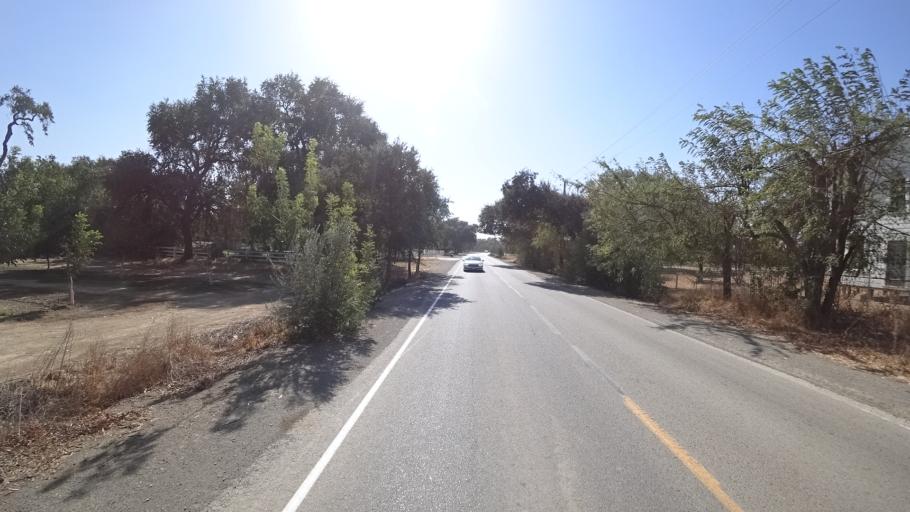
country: US
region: California
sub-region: Yolo County
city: Davis
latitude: 38.5274
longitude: -121.6946
